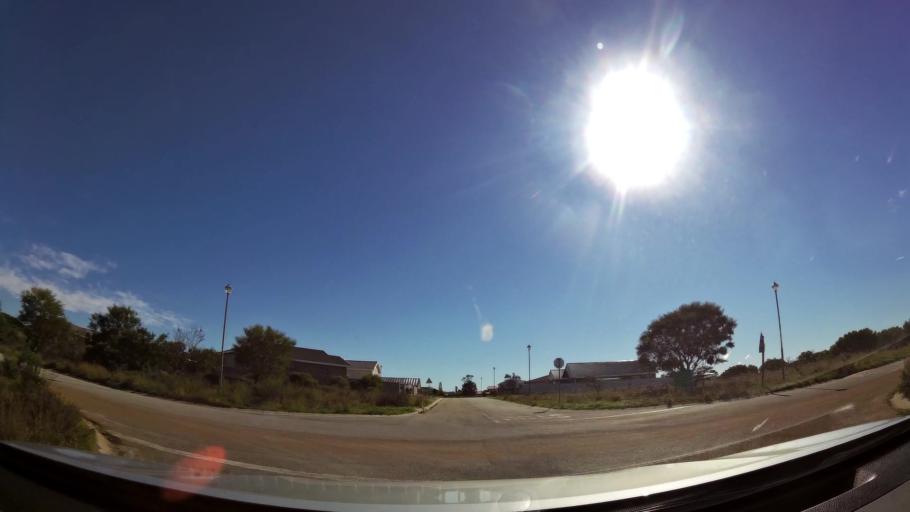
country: ZA
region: Eastern Cape
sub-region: Cacadu District Municipality
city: Jeffrey's Bay
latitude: -34.0344
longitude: 24.9085
